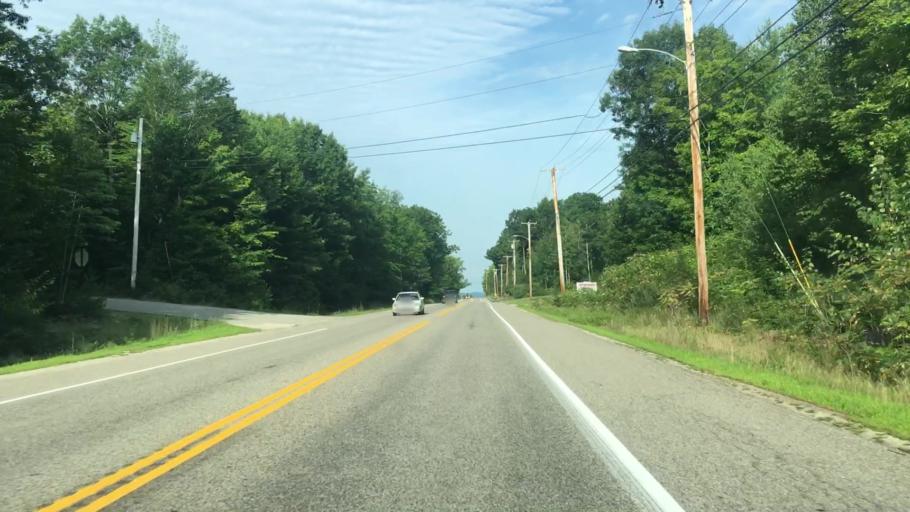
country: US
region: Maine
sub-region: Cumberland County
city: Steep Falls
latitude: 43.7336
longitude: -70.5665
